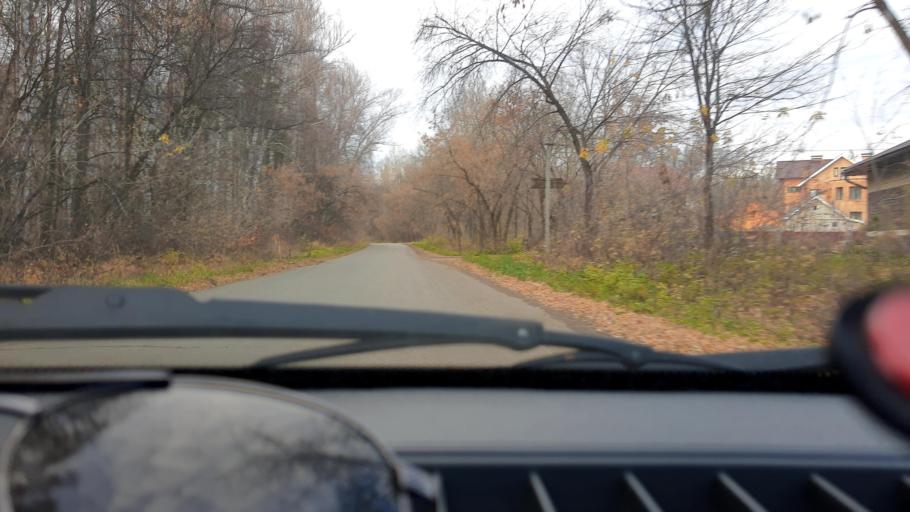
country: RU
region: Bashkortostan
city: Ufa
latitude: 54.7907
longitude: 56.1577
